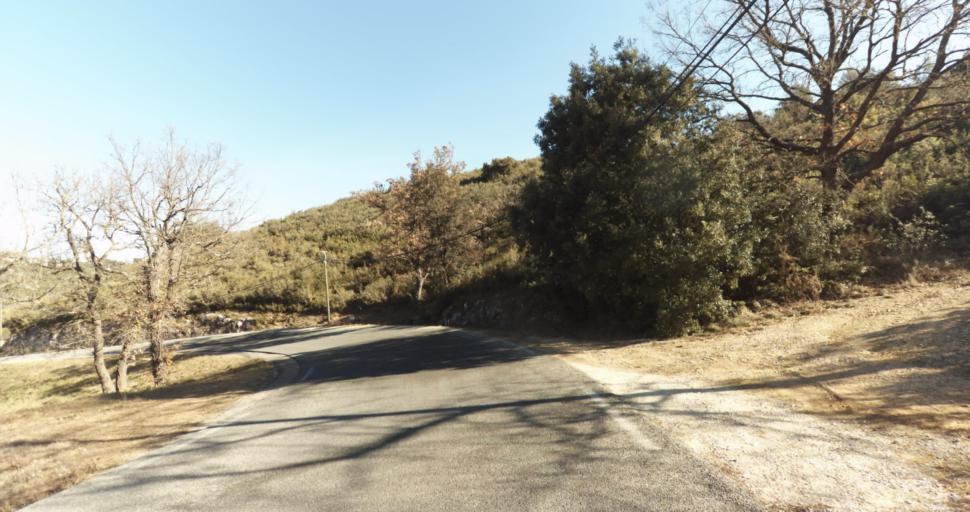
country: FR
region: Provence-Alpes-Cote d'Azur
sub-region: Departement des Bouches-du-Rhone
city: Peypin
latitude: 43.3800
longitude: 5.5673
